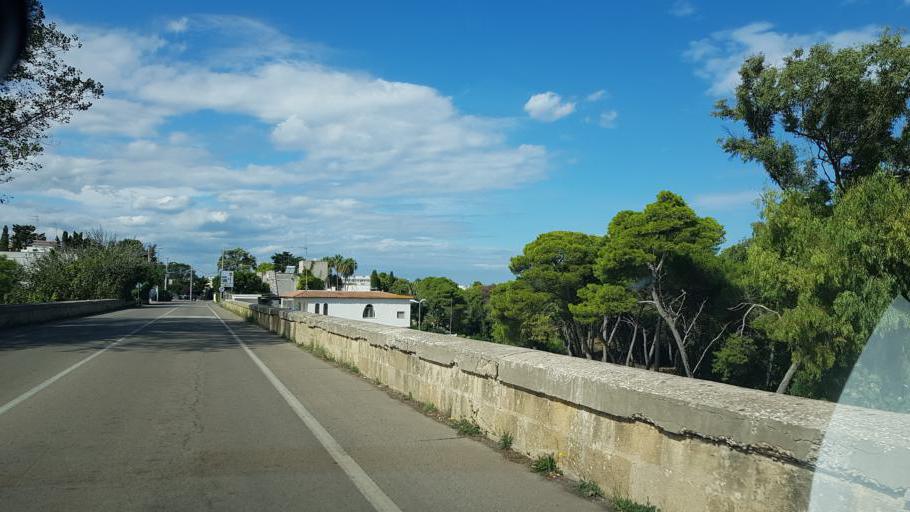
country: IT
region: Apulia
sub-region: Provincia di Lecce
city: Borgagne
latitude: 40.2691
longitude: 18.4306
